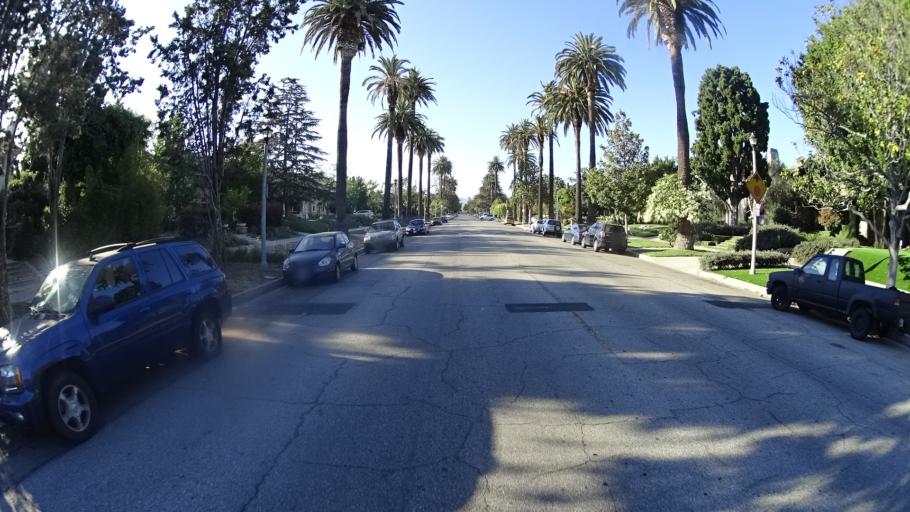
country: US
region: California
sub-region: Los Angeles County
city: Hollywood
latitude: 34.0702
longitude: -118.3156
